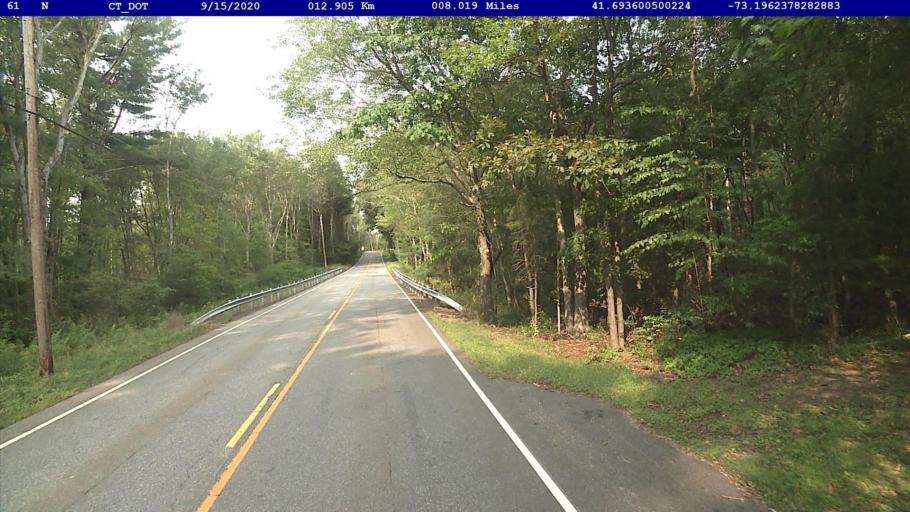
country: US
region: Connecticut
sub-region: Litchfield County
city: Bethlehem Village
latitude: 41.6936
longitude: -73.1962
